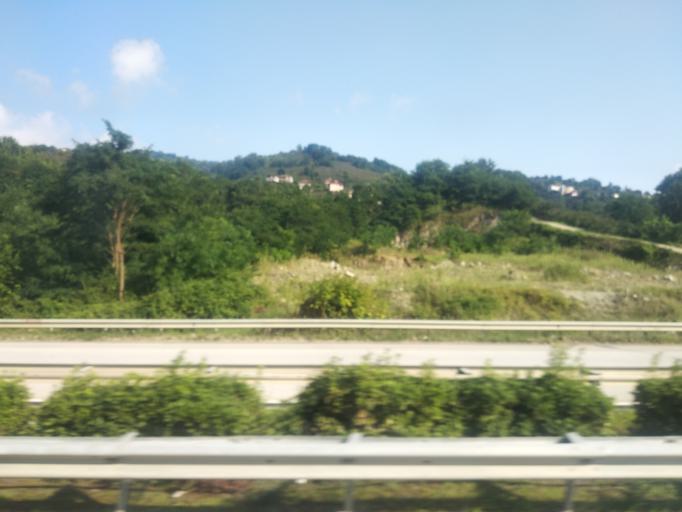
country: TR
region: Ordu
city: Ordu
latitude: 40.9995
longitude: 37.8221
